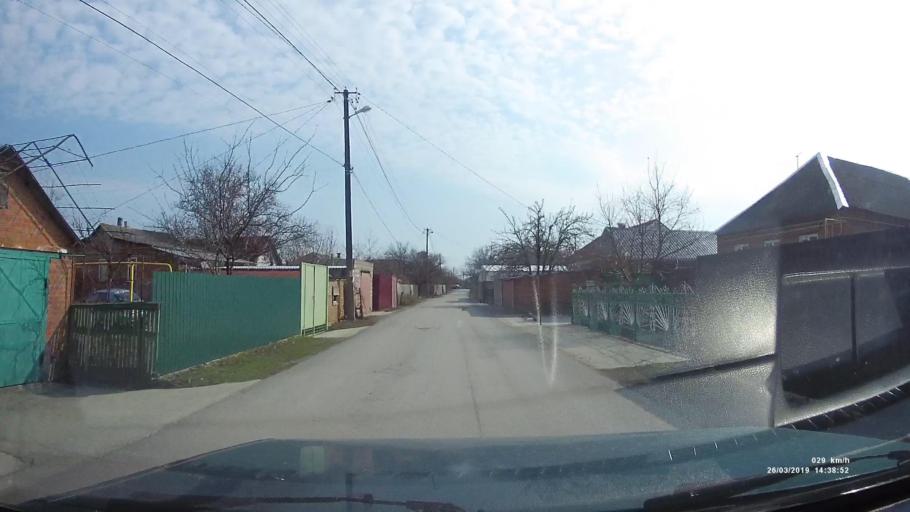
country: RU
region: Rostov
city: Novobessergenovka
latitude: 47.1807
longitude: 38.8623
